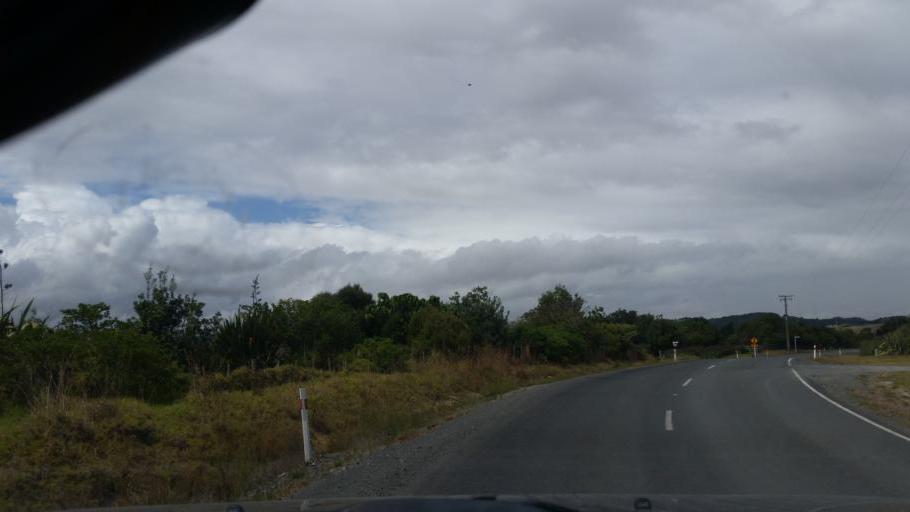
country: NZ
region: Auckland
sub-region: Auckland
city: Wellsford
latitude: -36.1365
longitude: 174.5580
